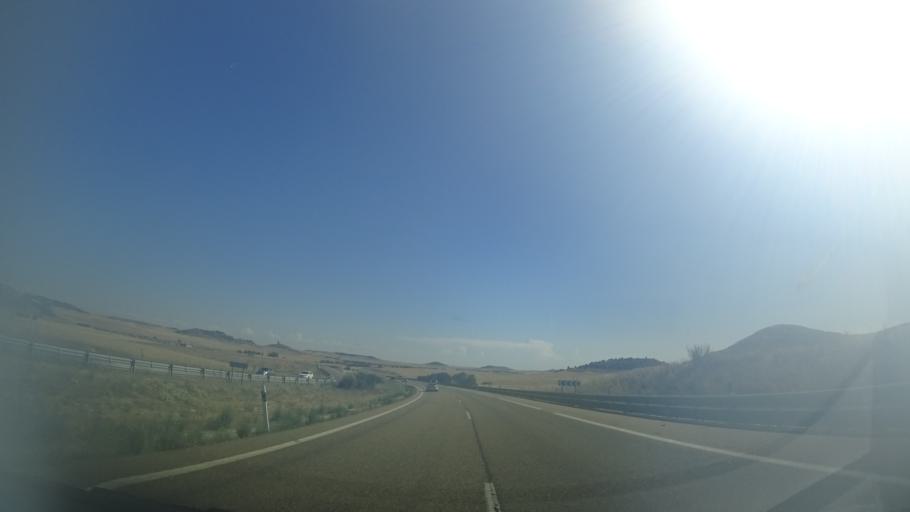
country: ES
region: Castille and Leon
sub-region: Provincia de Valladolid
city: Mota del Marques
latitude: 41.6641
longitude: -5.1982
